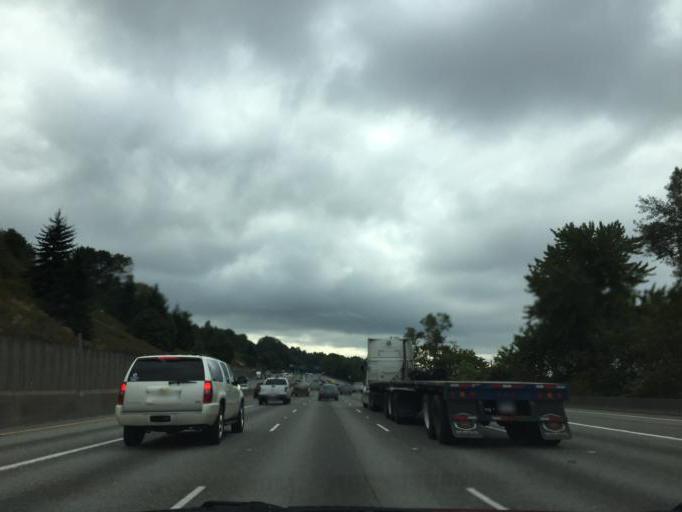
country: US
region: Washington
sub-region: King County
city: Tukwila
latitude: 47.4972
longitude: -122.2716
